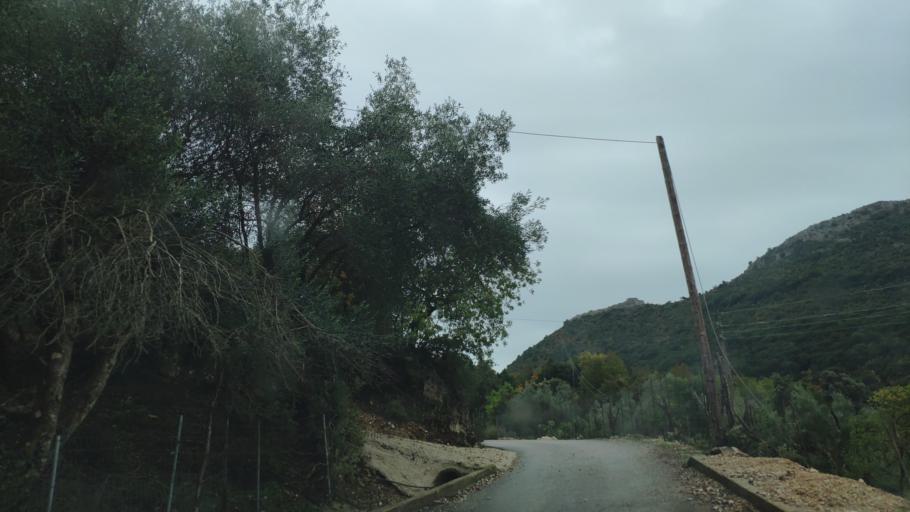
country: GR
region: Epirus
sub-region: Nomos Prevezis
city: Kanalaki
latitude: 39.3451
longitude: 20.6508
